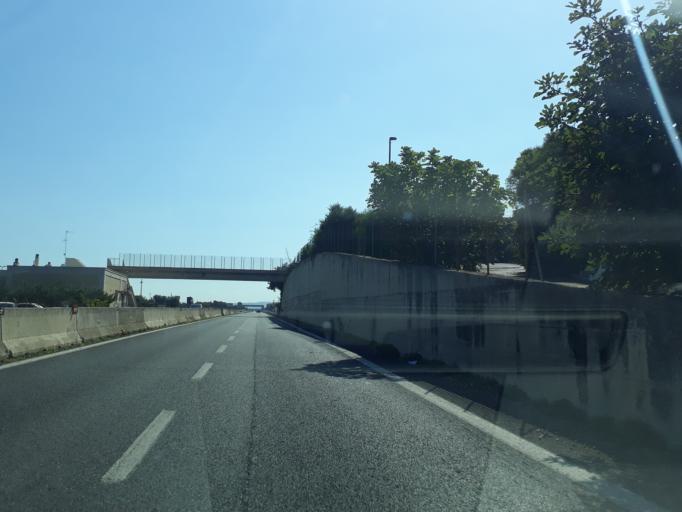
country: IT
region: Apulia
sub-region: Provincia di Brindisi
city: Fasano
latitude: 40.8915
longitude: 17.3324
